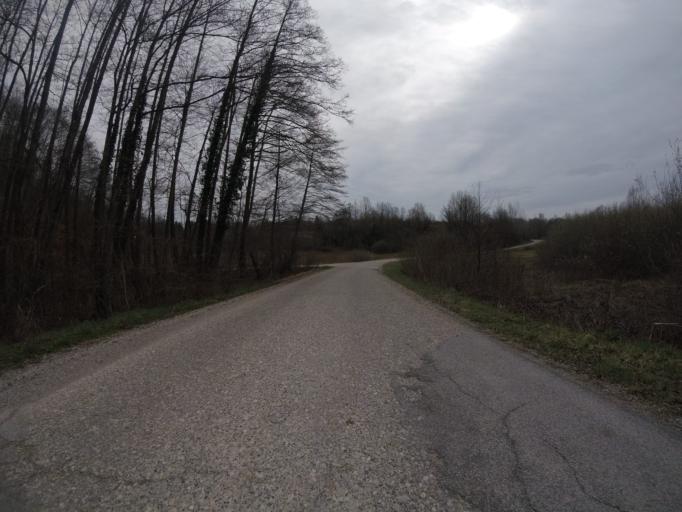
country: HR
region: Grad Zagreb
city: Strmec
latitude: 45.5942
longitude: 15.9180
